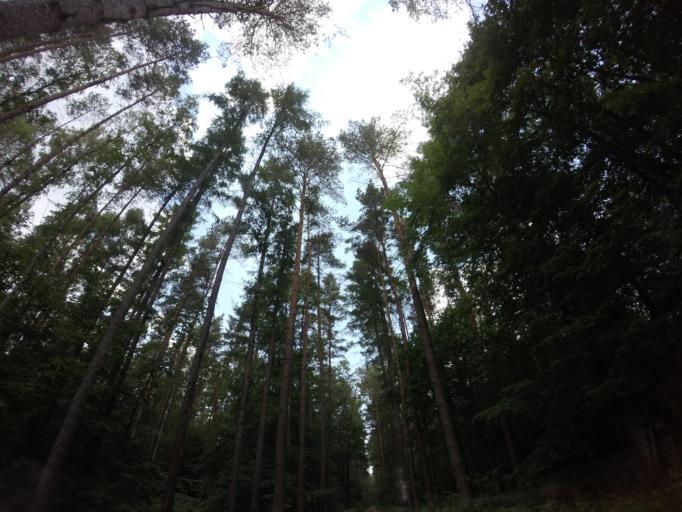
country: PL
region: West Pomeranian Voivodeship
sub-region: Powiat choszczenski
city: Bierzwnik
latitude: 53.0796
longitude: 15.6757
